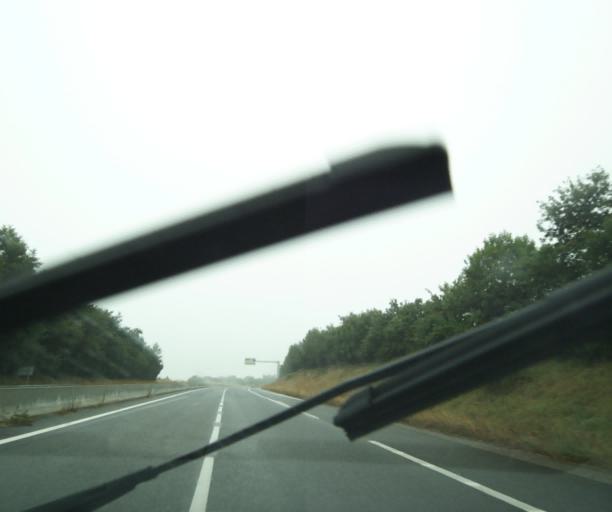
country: FR
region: Midi-Pyrenees
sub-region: Departement de l'Aveyron
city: Naucelle
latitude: 44.1399
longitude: 2.3127
